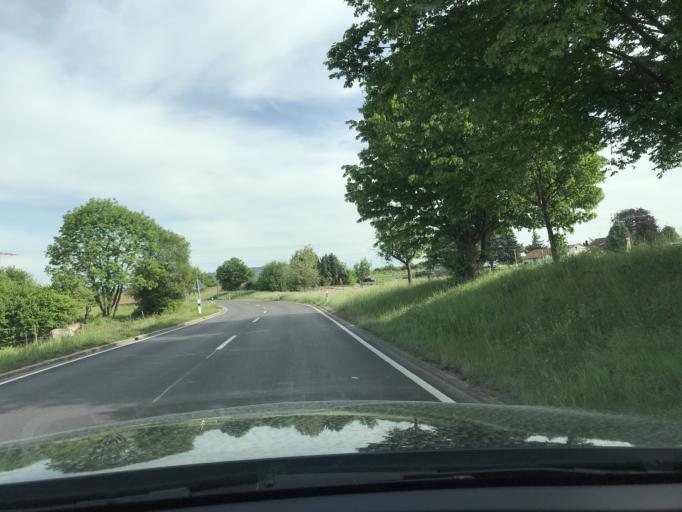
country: DE
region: Baden-Wuerttemberg
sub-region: Regierungsbezirk Stuttgart
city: Waiblingen
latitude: 48.8192
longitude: 9.3364
